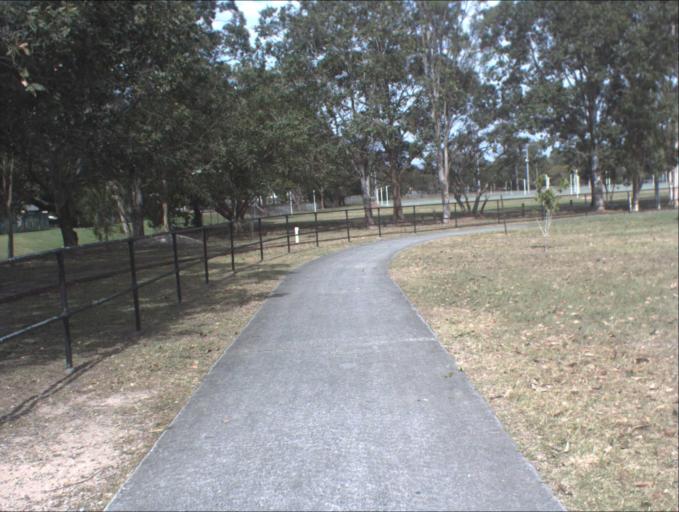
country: AU
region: Queensland
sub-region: Logan
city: Logan City
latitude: -27.6327
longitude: 153.1103
